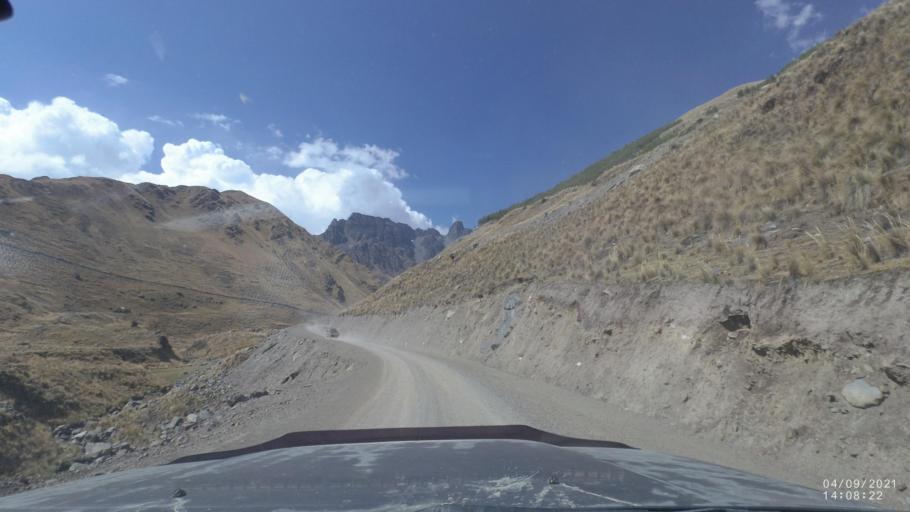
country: BO
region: Cochabamba
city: Sipe Sipe
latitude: -17.2263
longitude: -66.4634
